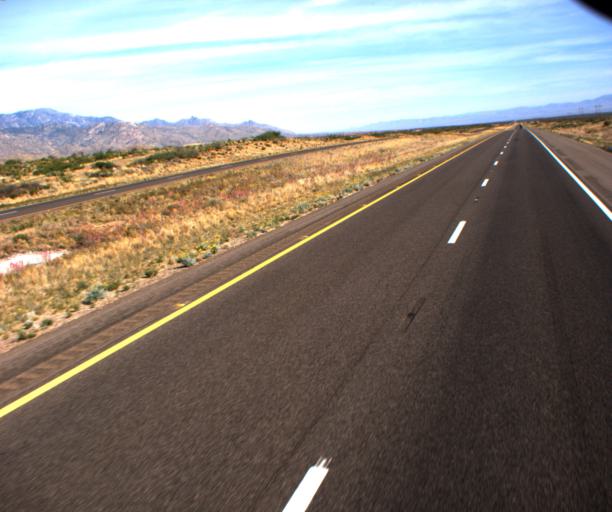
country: US
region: Arizona
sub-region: Graham County
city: Swift Trail Junction
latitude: 32.5660
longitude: -109.6799
